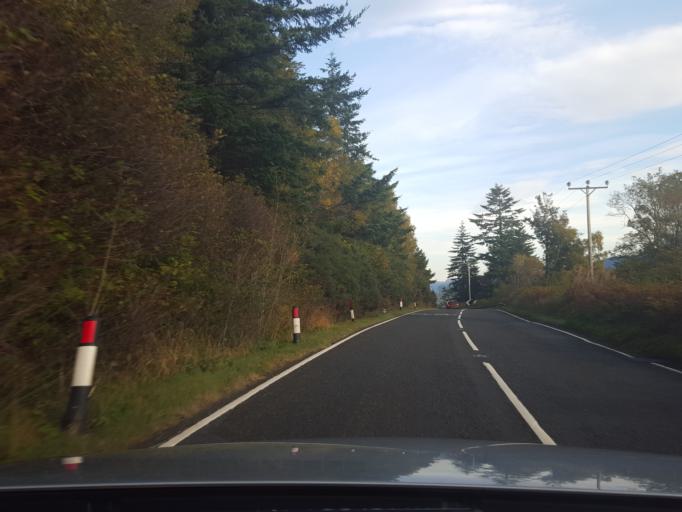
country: GB
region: Scotland
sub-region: Highland
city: Beauly
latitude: 57.2236
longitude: -4.5754
